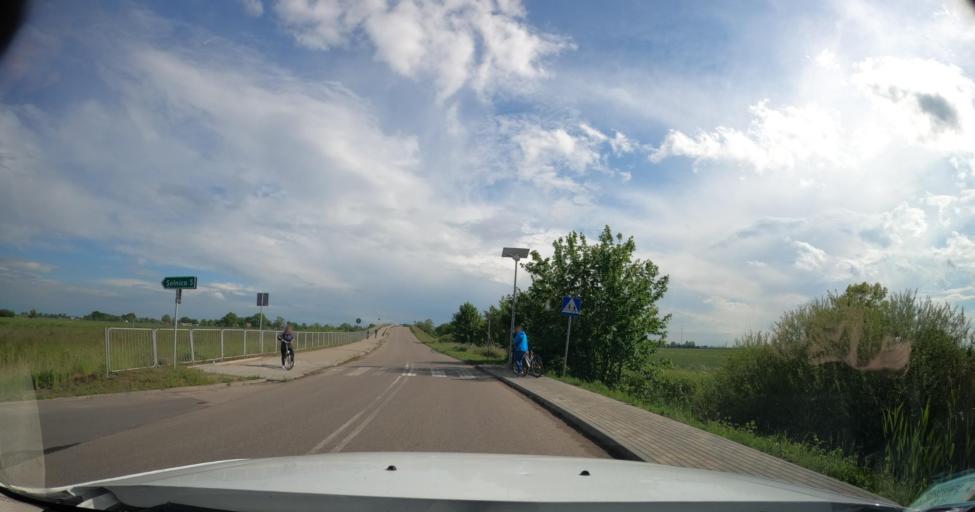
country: PL
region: Pomeranian Voivodeship
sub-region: Powiat nowodworski
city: Nowy Dwor Gdanski
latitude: 54.1965
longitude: 19.1399
